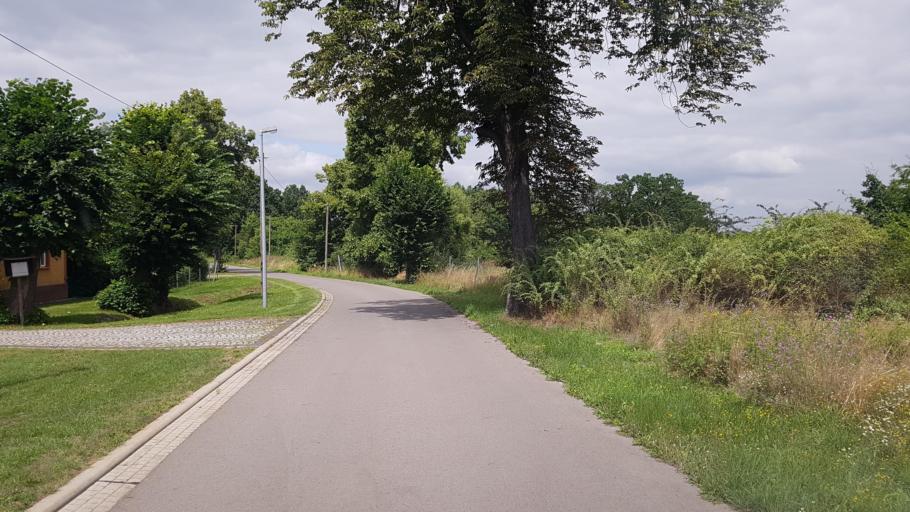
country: DE
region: Brandenburg
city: Altdobern
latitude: 51.6509
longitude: 14.0799
